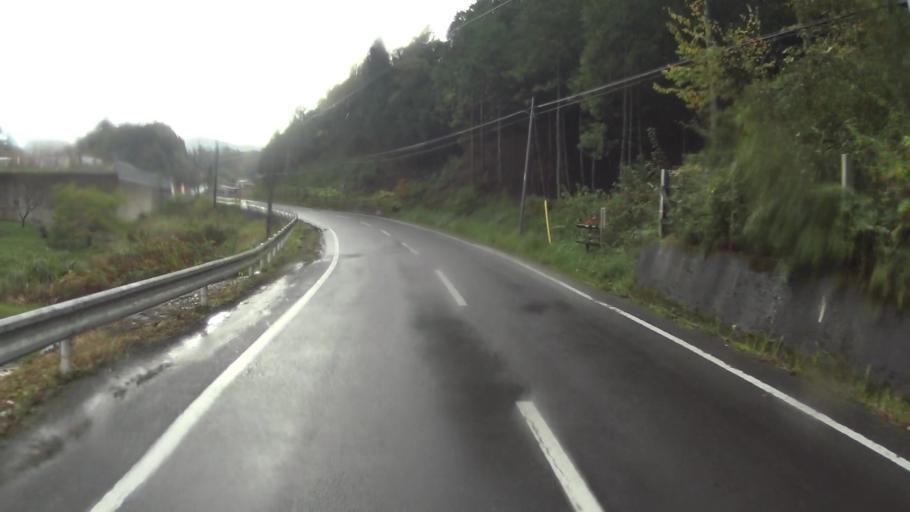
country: JP
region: Kyoto
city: Ayabe
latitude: 35.2895
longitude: 135.2411
